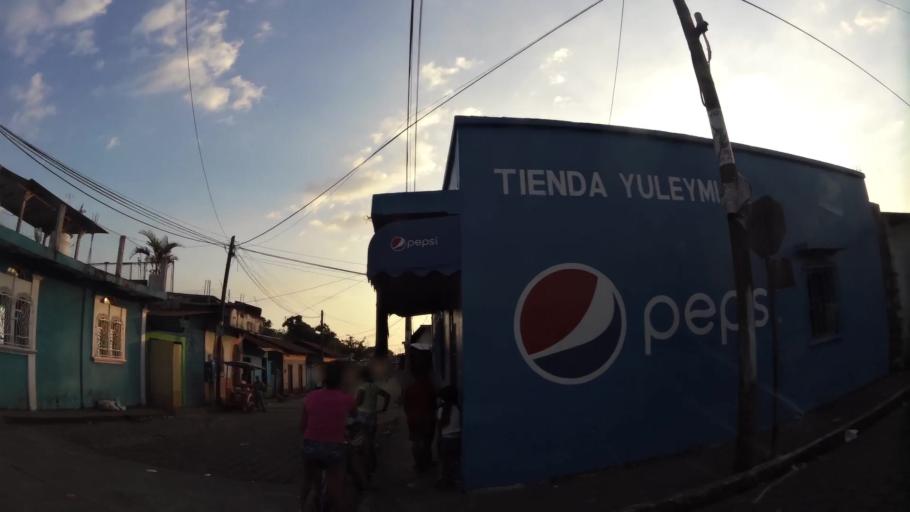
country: GT
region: Retalhuleu
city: San Sebastian
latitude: 14.5592
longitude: -91.6488
